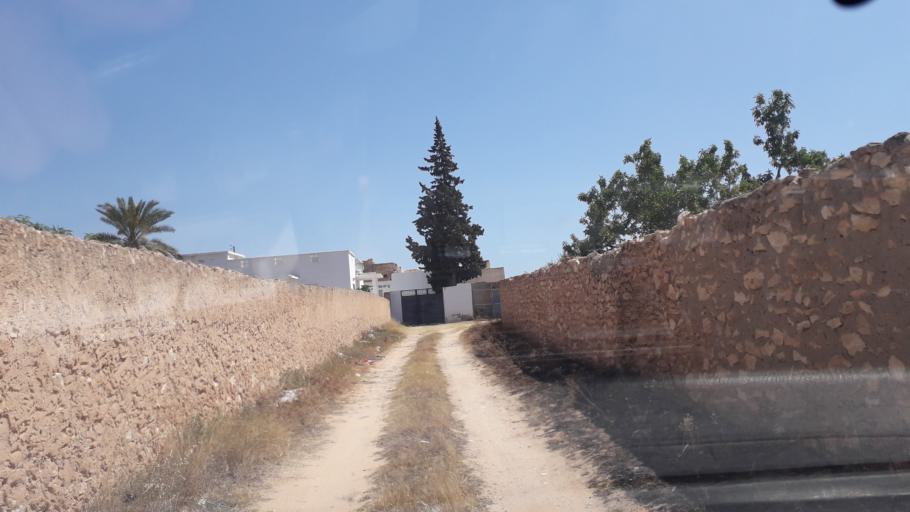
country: TN
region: Safaqis
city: Al Qarmadah
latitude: 34.8208
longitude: 10.7684
